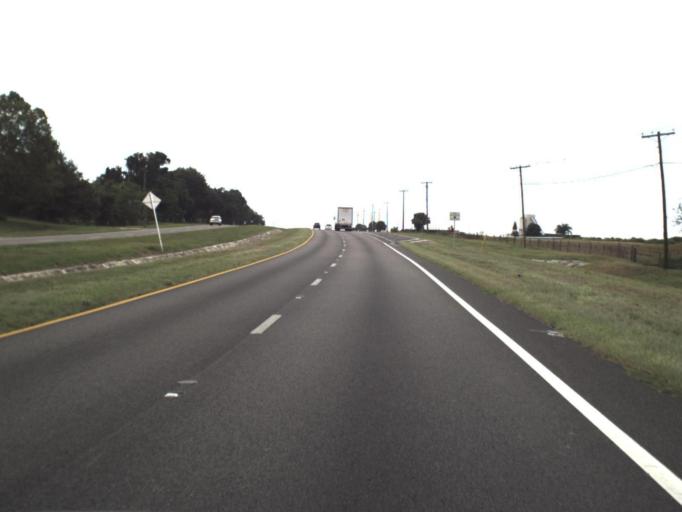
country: US
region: Florida
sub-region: Polk County
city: Bartow
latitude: 27.8587
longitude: -81.8285
